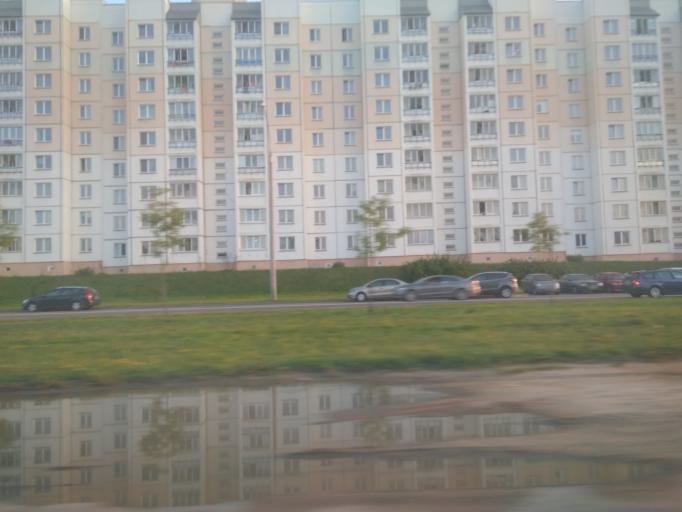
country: BY
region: Minsk
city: Novoye Medvezhino
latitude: 53.9210
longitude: 27.4625
